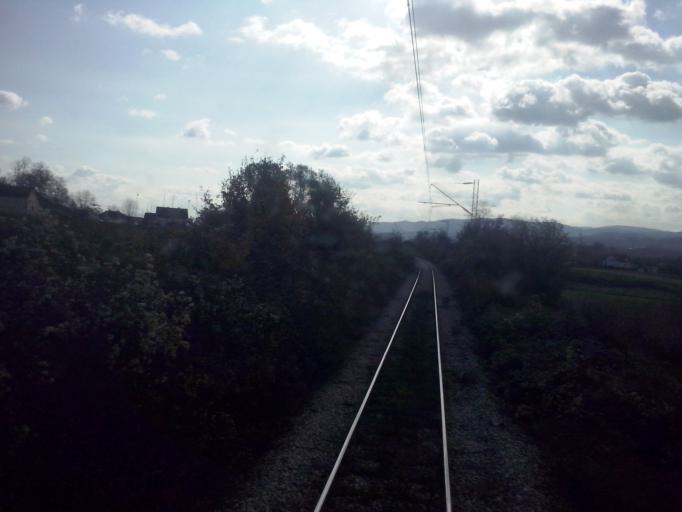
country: RS
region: Central Serbia
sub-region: Zlatiborski Okrug
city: Pozega
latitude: 43.8764
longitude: 20.0000
